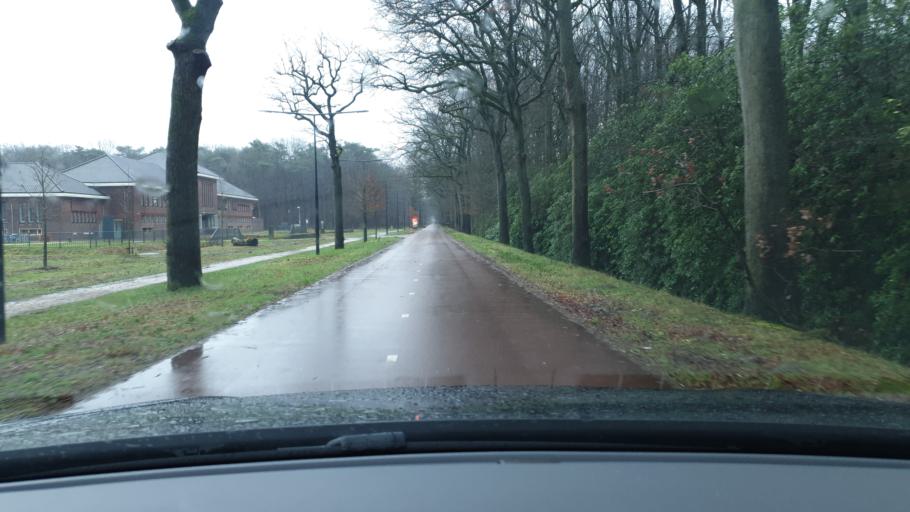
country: NL
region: North Brabant
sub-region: Gemeente Eindhoven
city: Meerhoven
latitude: 51.4601
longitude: 5.4290
